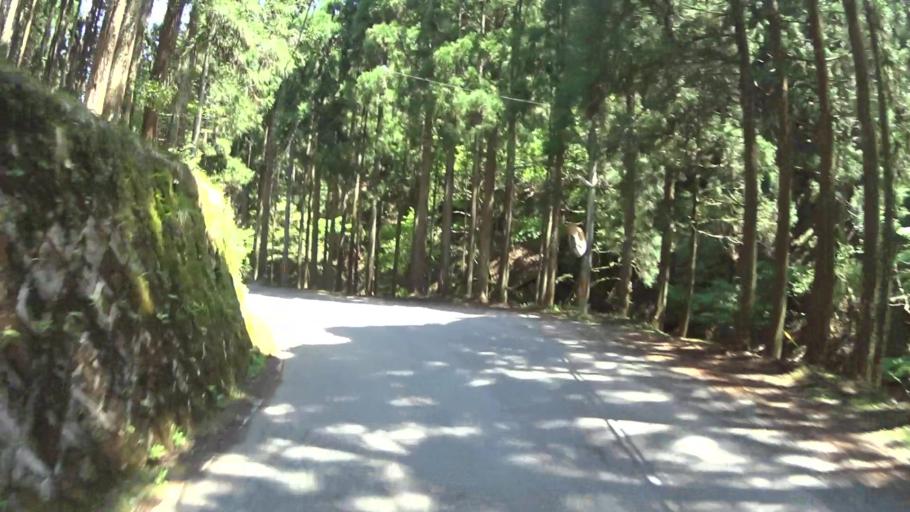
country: JP
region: Shiga Prefecture
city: Kitahama
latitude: 35.1863
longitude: 135.7846
